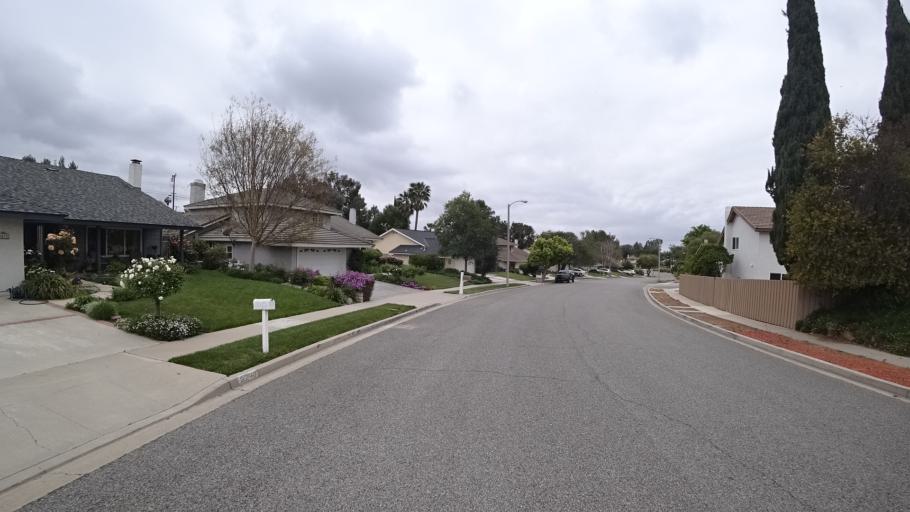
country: US
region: California
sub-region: Ventura County
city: Thousand Oaks
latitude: 34.2152
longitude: -118.8840
